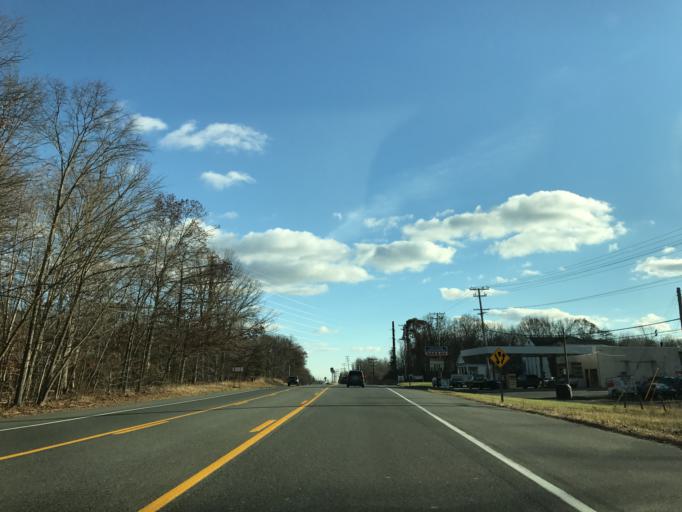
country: US
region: Maryland
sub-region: Harford County
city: Fallston
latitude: 39.5049
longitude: -76.4019
